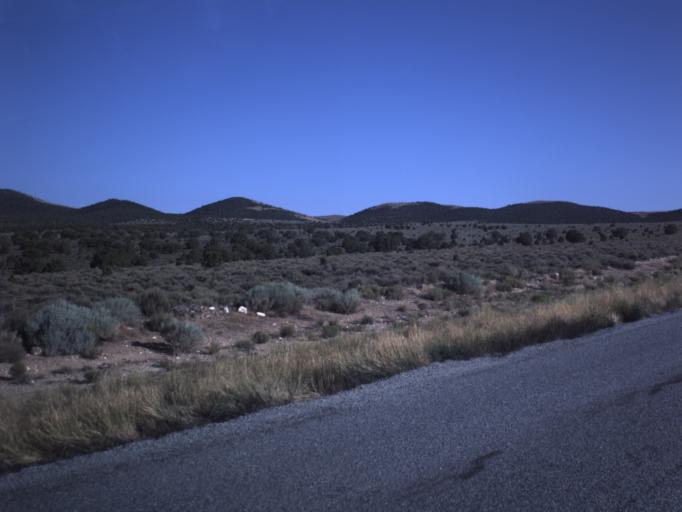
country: US
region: Utah
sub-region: Iron County
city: Parowan
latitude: 38.0213
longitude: -112.9981
